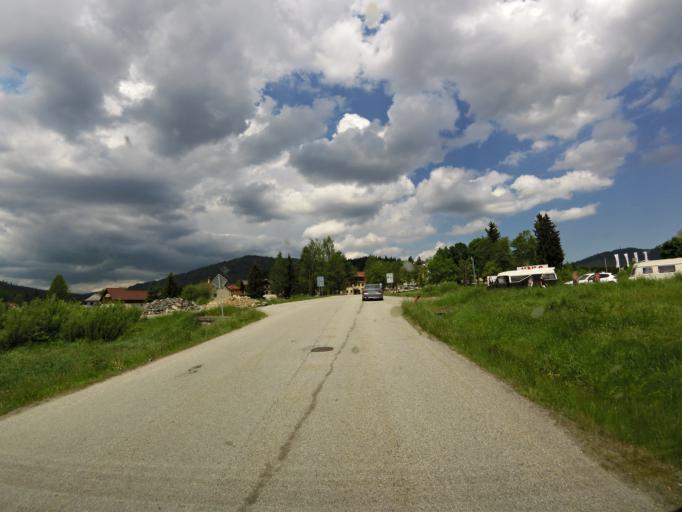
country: DE
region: Bavaria
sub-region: Lower Bavaria
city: Philippsreut
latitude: 48.9060
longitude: 13.7218
